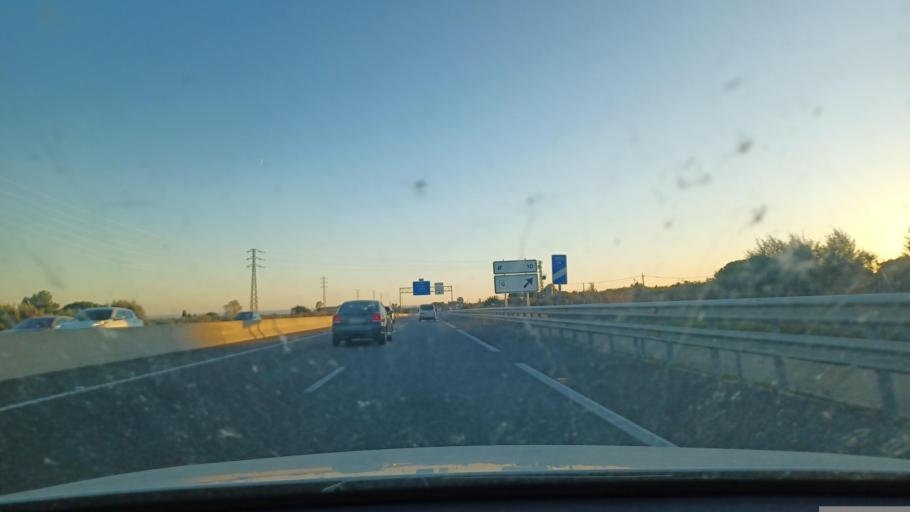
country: ES
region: Catalonia
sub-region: Provincia de Tarragona
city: La Selva
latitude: 41.1888
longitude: 1.1375
